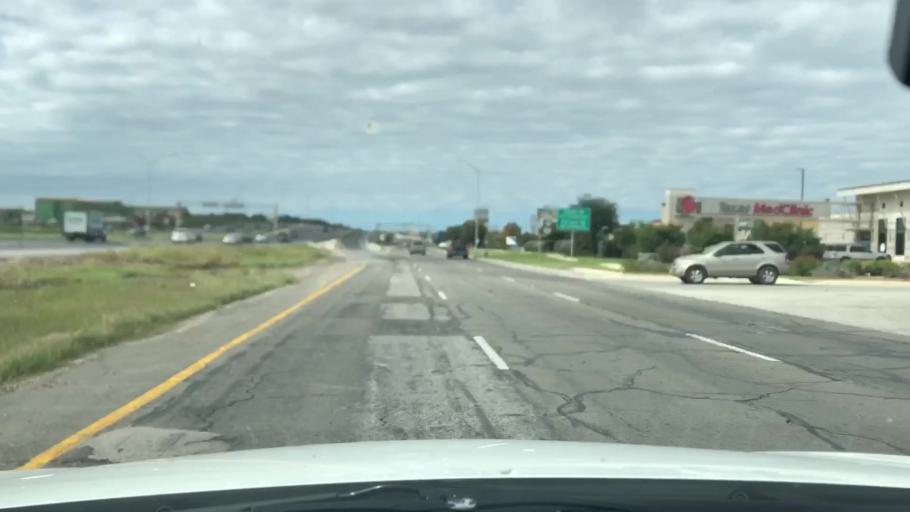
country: US
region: Texas
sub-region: Bexar County
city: Lackland Air Force Base
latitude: 29.4374
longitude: -98.6539
